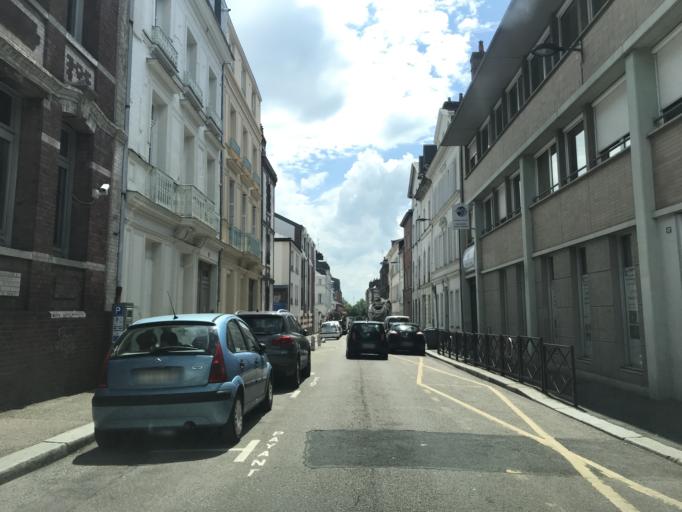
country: FR
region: Haute-Normandie
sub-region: Departement de la Seine-Maritime
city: Rouen
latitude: 49.4445
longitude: 1.0813
